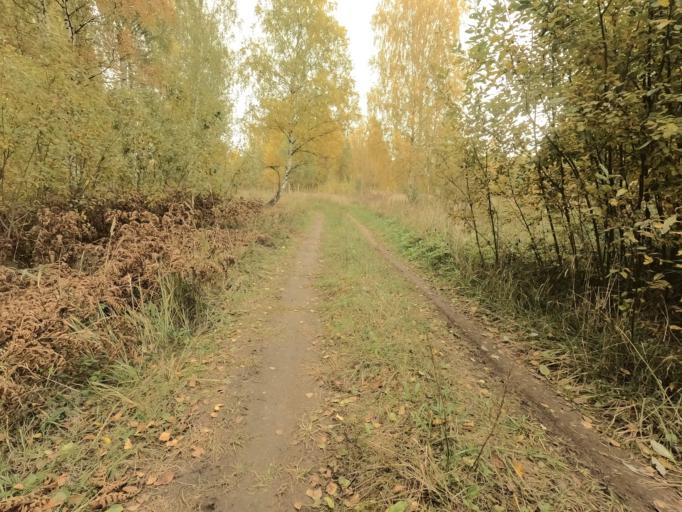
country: RU
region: Novgorod
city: Pankovka
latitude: 58.8652
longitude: 30.9309
